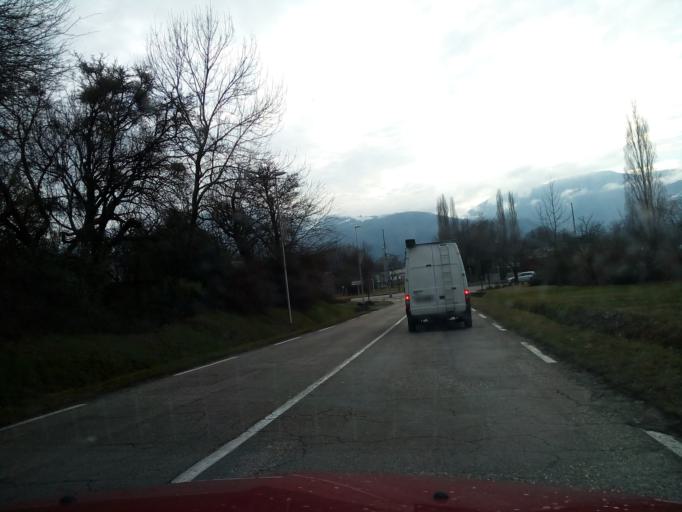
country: FR
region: Rhone-Alpes
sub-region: Departement de l'Isere
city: Corenc
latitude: 45.2105
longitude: 5.7816
